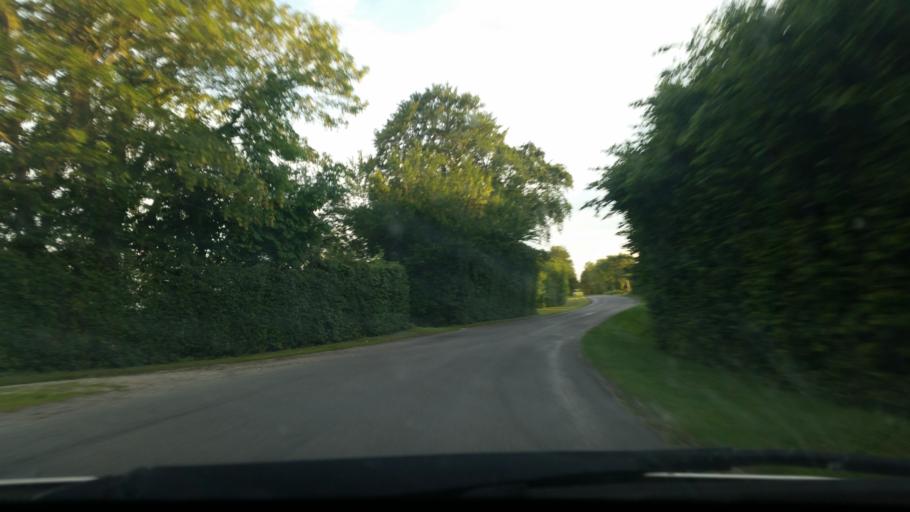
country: DK
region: Central Jutland
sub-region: Samso Kommune
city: Tranebjerg
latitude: 55.8392
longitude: 10.6138
